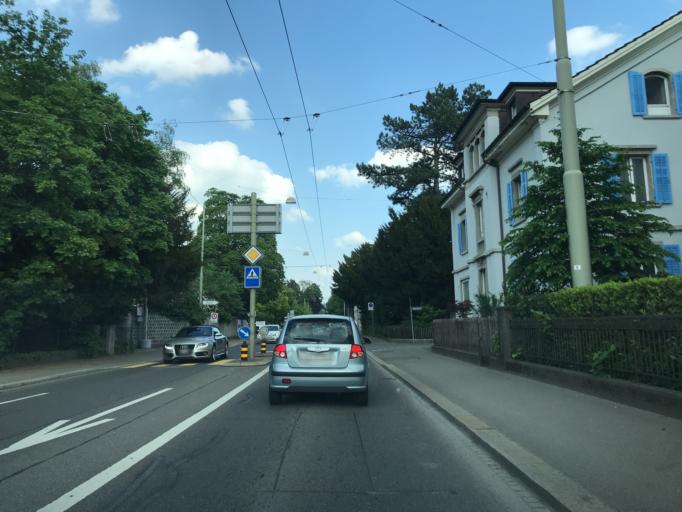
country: CH
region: Zurich
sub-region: Bezirk Winterthur
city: Mattenbach (Kreis 7) / Deutweg
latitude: 47.4982
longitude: 8.7351
